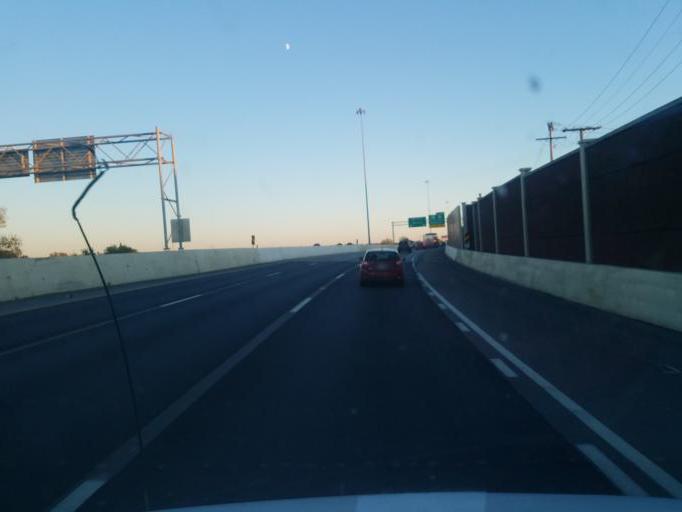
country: US
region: Ohio
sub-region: Stark County
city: Canton
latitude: 40.7972
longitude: -81.3911
